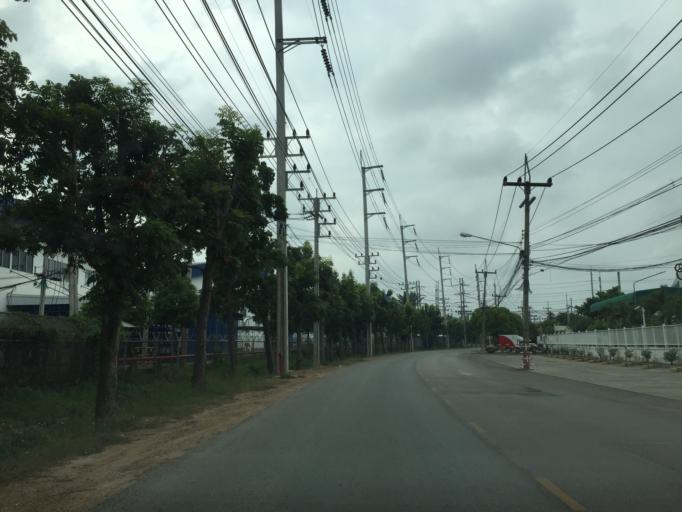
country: TH
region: Lamphun
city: Lamphun
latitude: 18.5923
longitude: 99.0472
